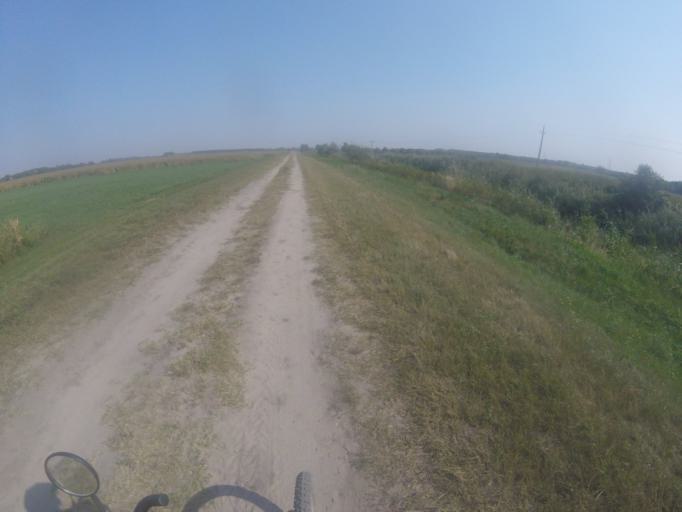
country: HU
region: Bacs-Kiskun
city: Ersekcsanad
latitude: 46.2199
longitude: 18.9559
